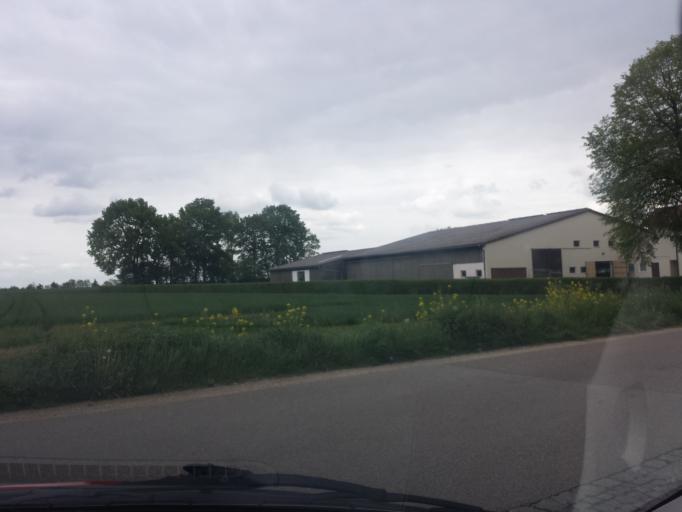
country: DE
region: Bavaria
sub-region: Upper Bavaria
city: Hepberg
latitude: 48.8286
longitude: 11.4665
